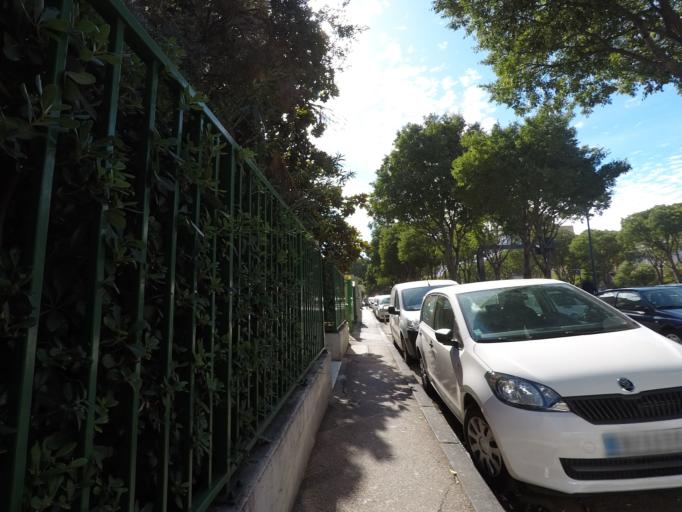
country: FR
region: Provence-Alpes-Cote d'Azur
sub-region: Departement des Bouches-du-Rhone
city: Marseille 08
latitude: 43.2717
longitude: 5.3902
